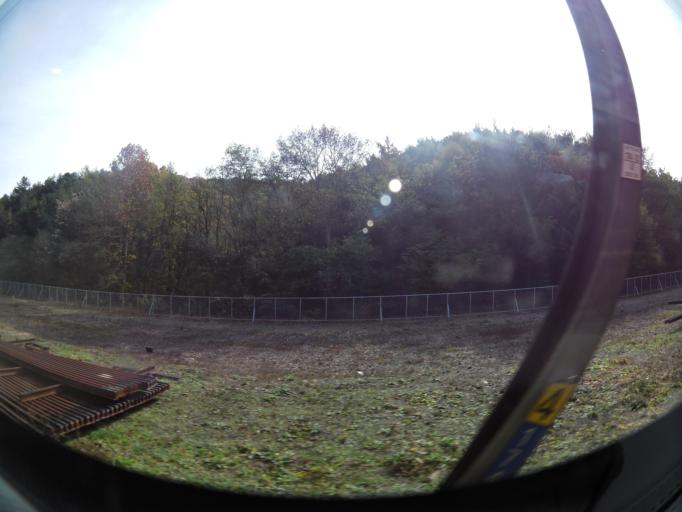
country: KR
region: Daejeon
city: Daejeon
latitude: 36.3376
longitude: 127.4927
